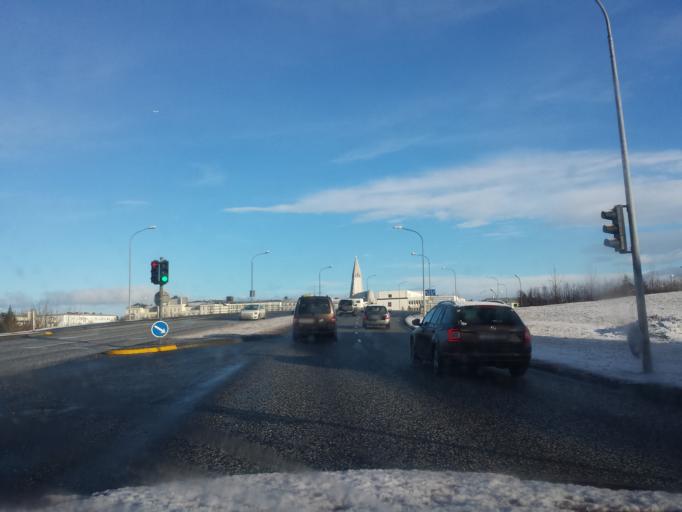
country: IS
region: Capital Region
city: Kopavogur
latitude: 64.1350
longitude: -21.9231
